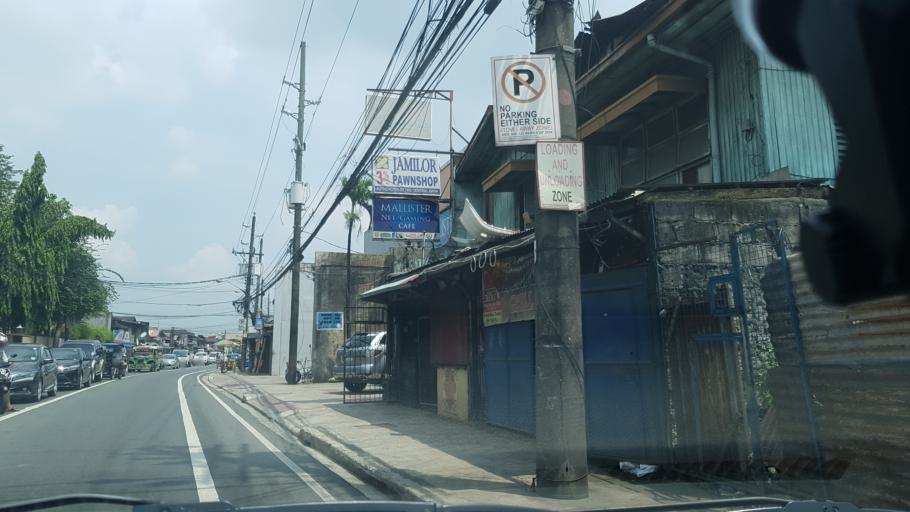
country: PH
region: Metro Manila
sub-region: Marikina
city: Calumpang
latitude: 14.6536
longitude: 121.1032
